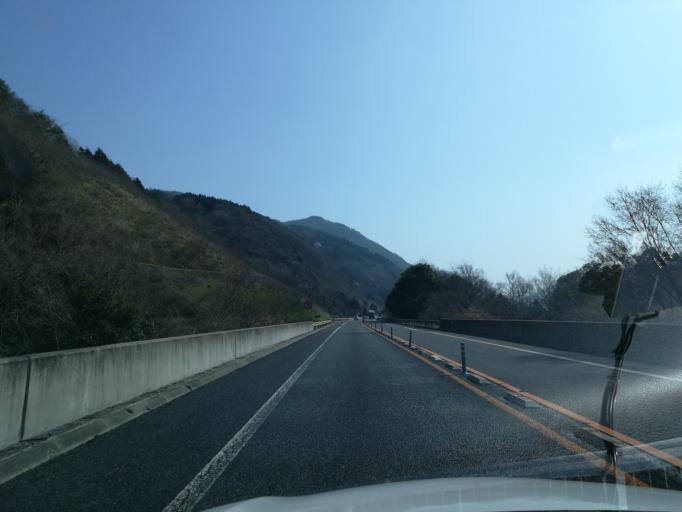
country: JP
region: Tokushima
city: Ikedacho
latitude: 34.0093
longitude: 133.7256
